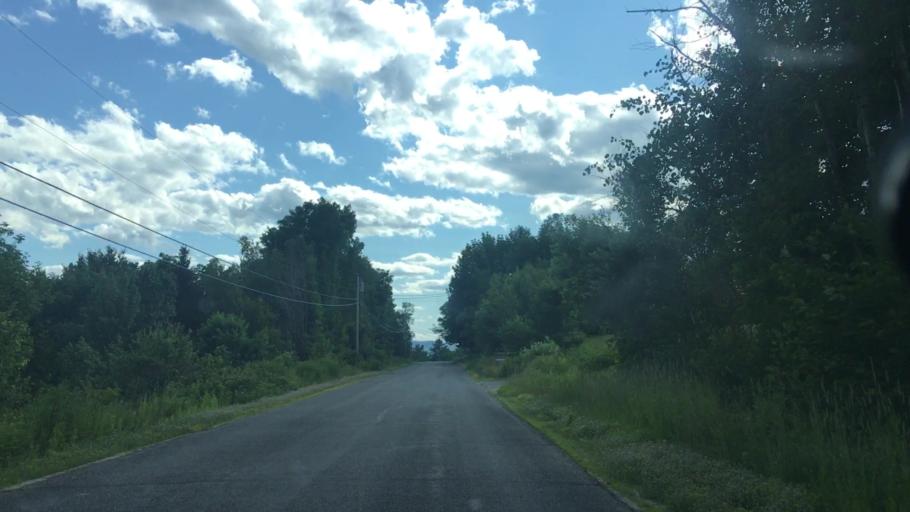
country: US
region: Maine
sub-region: Franklin County
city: Wilton
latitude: 44.6262
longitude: -70.2097
